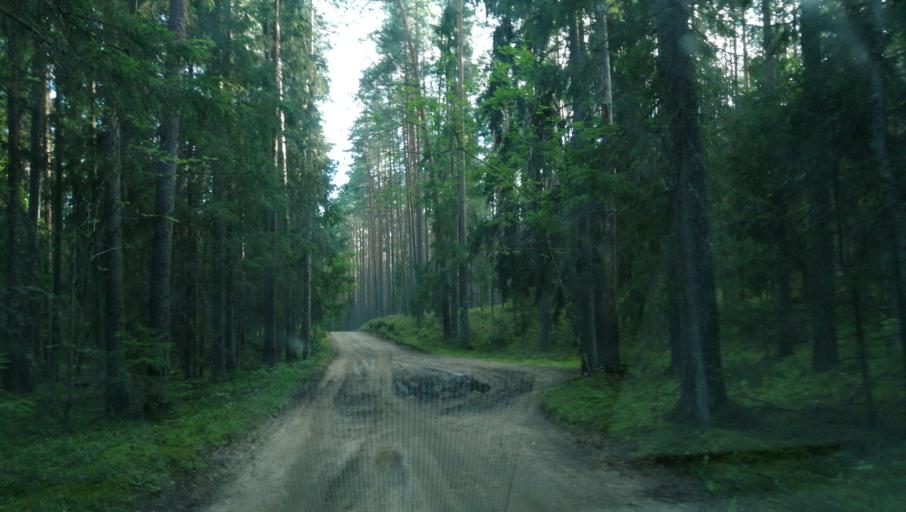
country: LV
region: Cesu Rajons
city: Cesis
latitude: 57.2962
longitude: 25.2073
